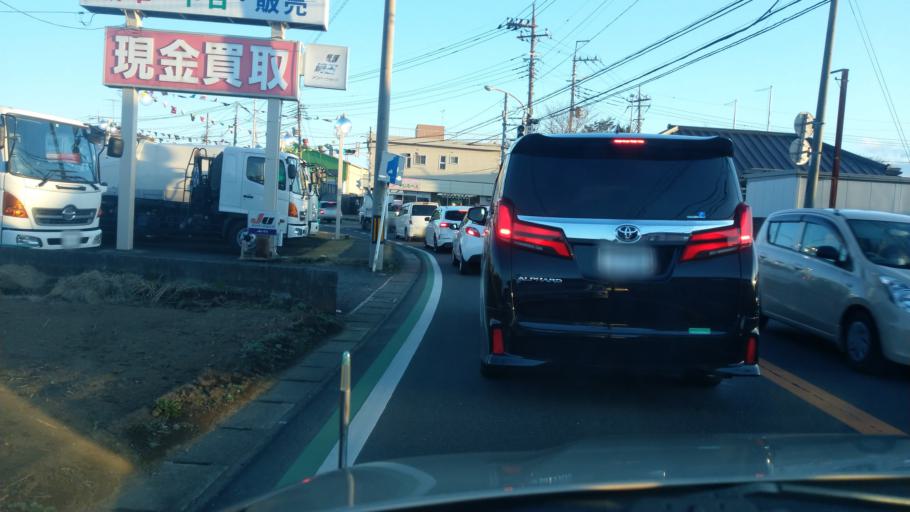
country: JP
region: Saitama
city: Ageoshimo
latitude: 35.9385
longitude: 139.5722
